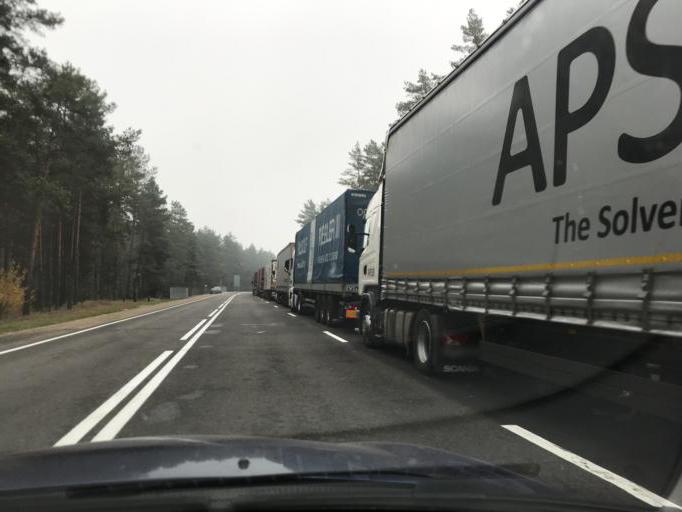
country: LT
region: Alytaus apskritis
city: Druskininkai
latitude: 53.9371
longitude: 23.9542
